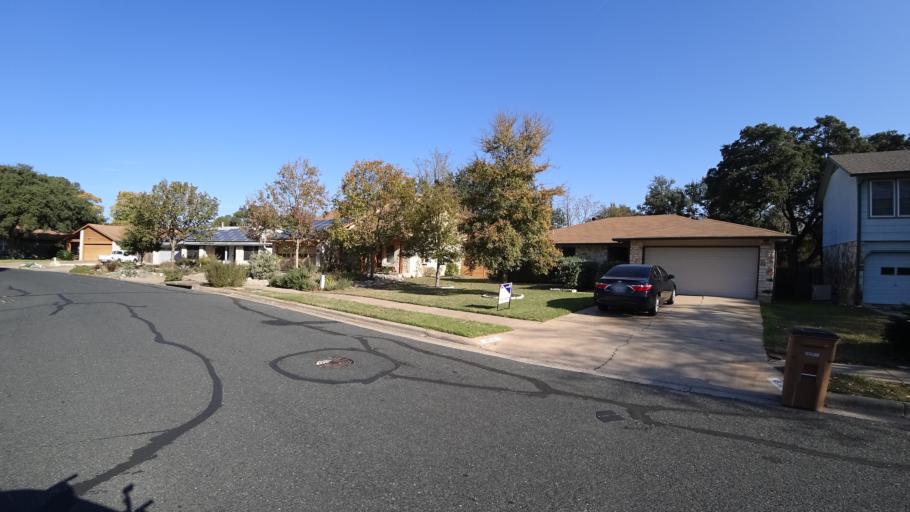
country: US
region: Texas
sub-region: Travis County
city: Barton Creek
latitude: 30.2274
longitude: -97.8389
